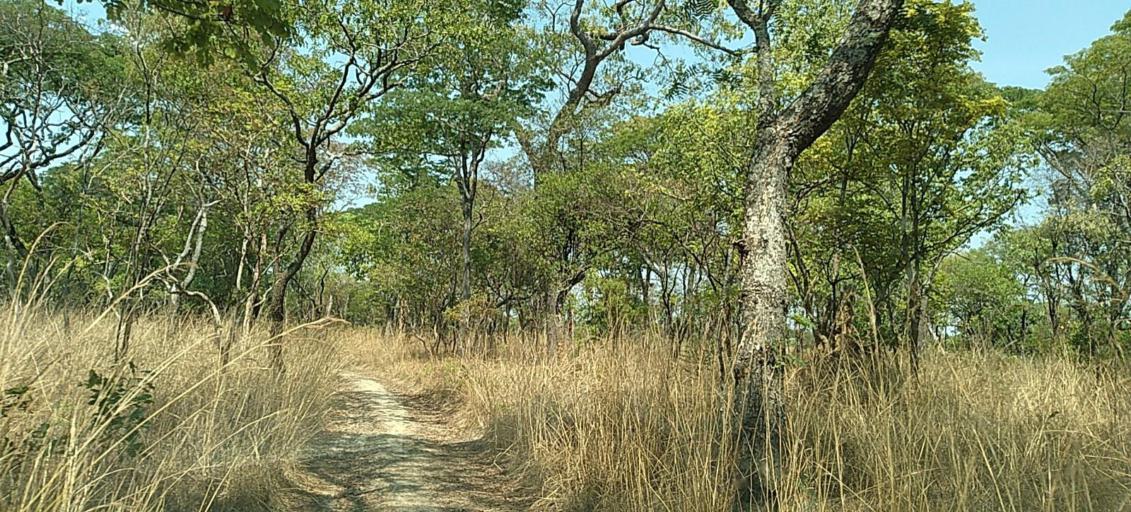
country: ZM
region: Copperbelt
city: Mpongwe
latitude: -13.7944
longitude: 28.0868
